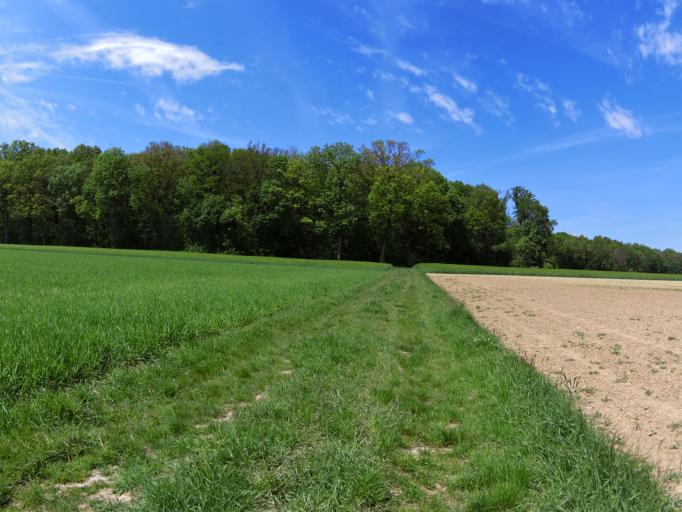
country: DE
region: Bavaria
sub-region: Regierungsbezirk Unterfranken
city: Theilheim
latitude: 49.7427
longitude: 10.0369
